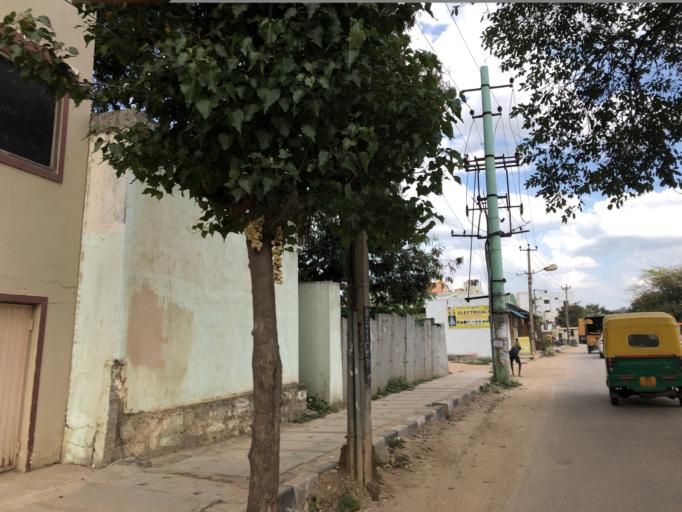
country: IN
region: Karnataka
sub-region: Bangalore Urban
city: Bangalore
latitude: 12.9913
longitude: 77.6917
